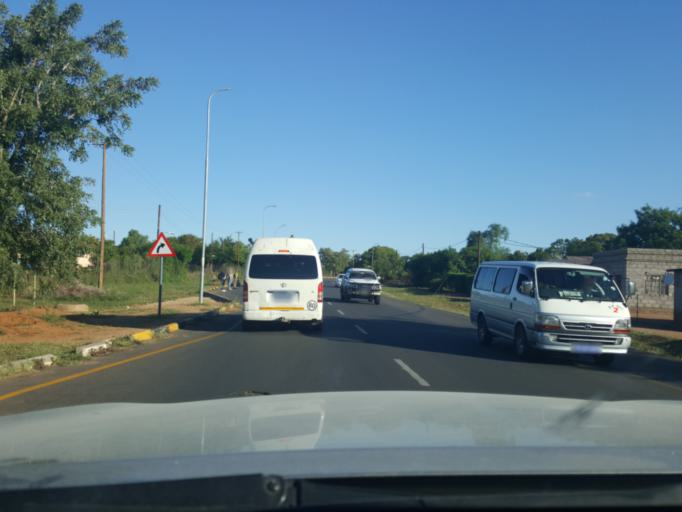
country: BW
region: South East
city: Gaborone
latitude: -24.6393
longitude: 25.9395
